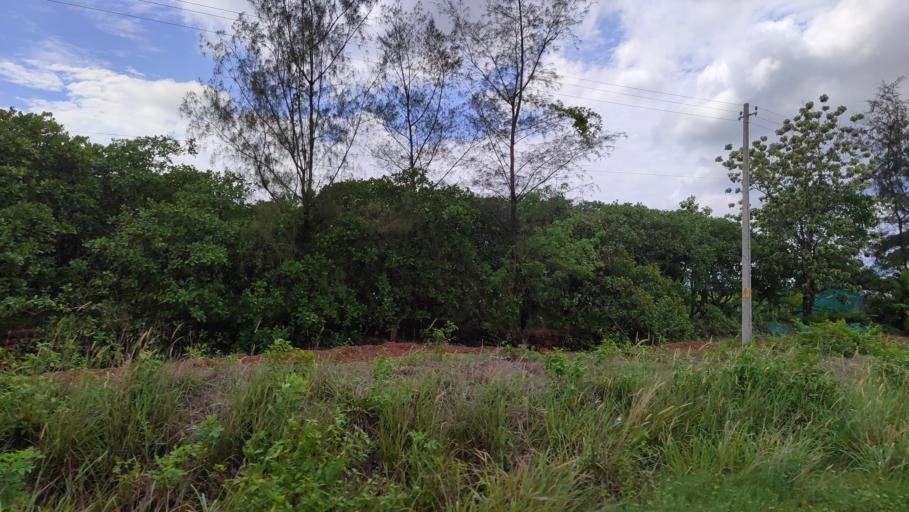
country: IN
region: Kerala
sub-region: Kasaragod District
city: Kannangad
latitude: 12.3976
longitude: 75.0967
